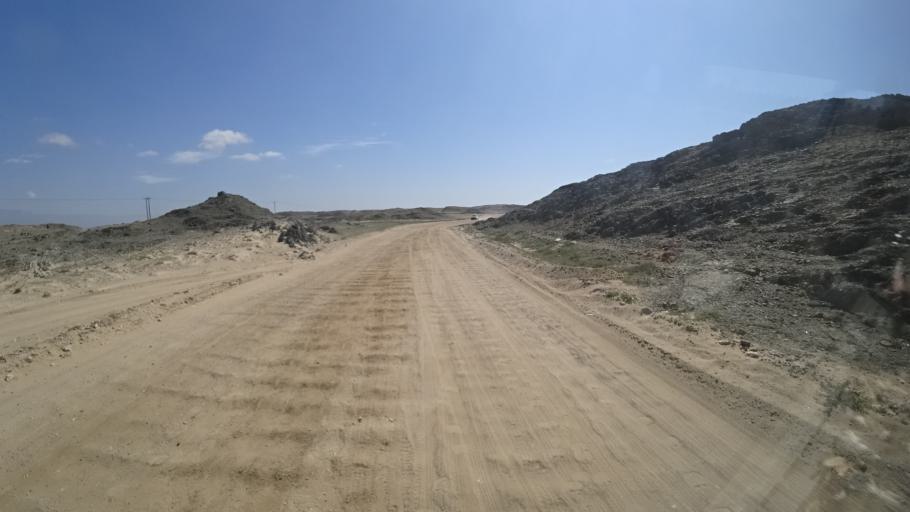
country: OM
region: Zufar
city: Salalah
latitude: 16.9641
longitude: 54.7754
